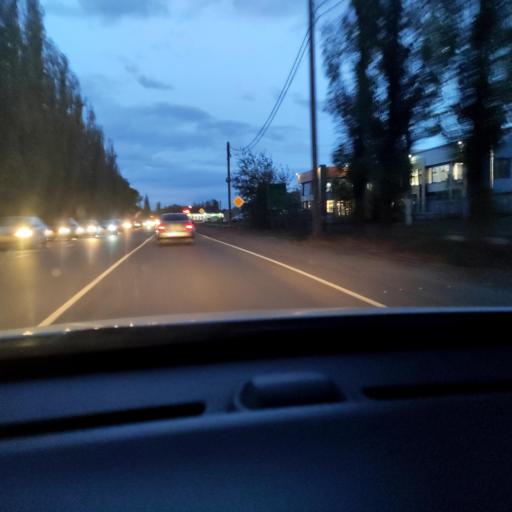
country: RU
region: Voronezj
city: Maslovka
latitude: 51.6227
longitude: 39.2465
